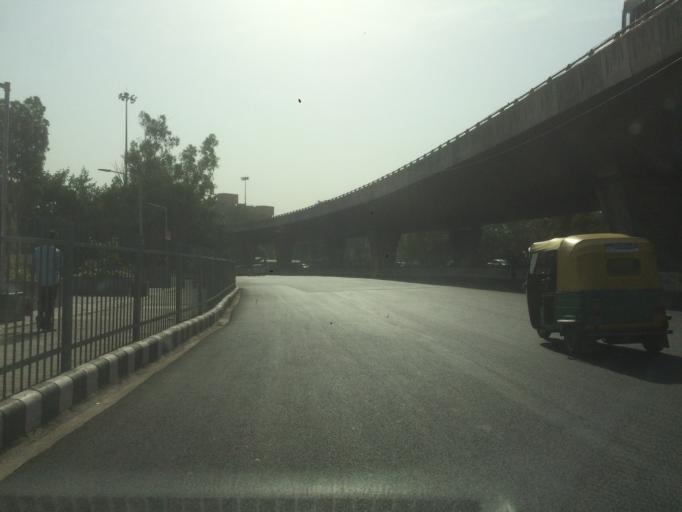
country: IN
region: NCT
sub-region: New Delhi
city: New Delhi
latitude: 28.5659
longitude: 77.2508
